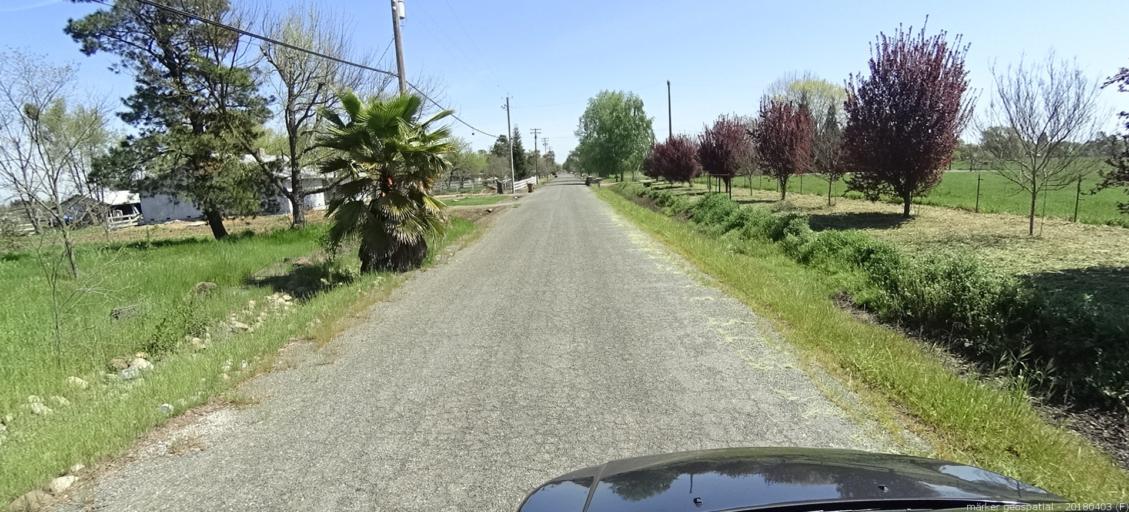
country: US
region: California
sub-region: Sacramento County
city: Wilton
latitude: 38.3873
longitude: -121.2686
